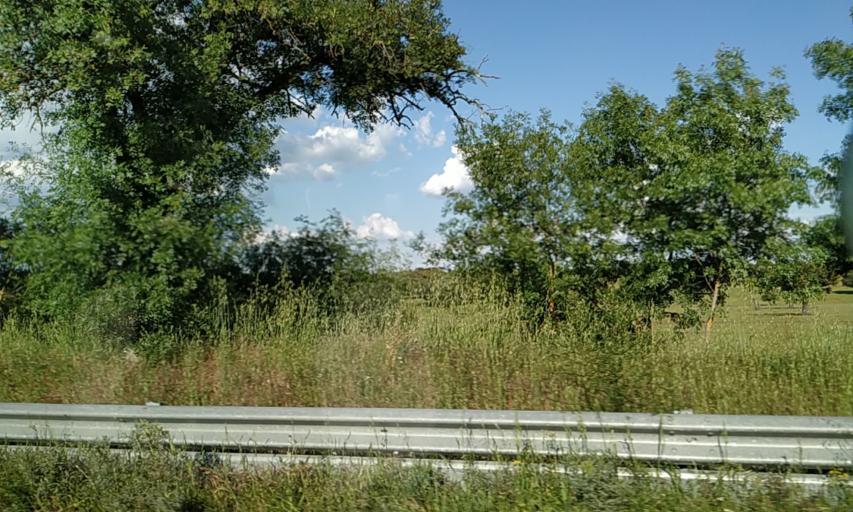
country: PT
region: Portalegre
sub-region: Portalegre
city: Urra
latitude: 39.1593
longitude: -7.4542
